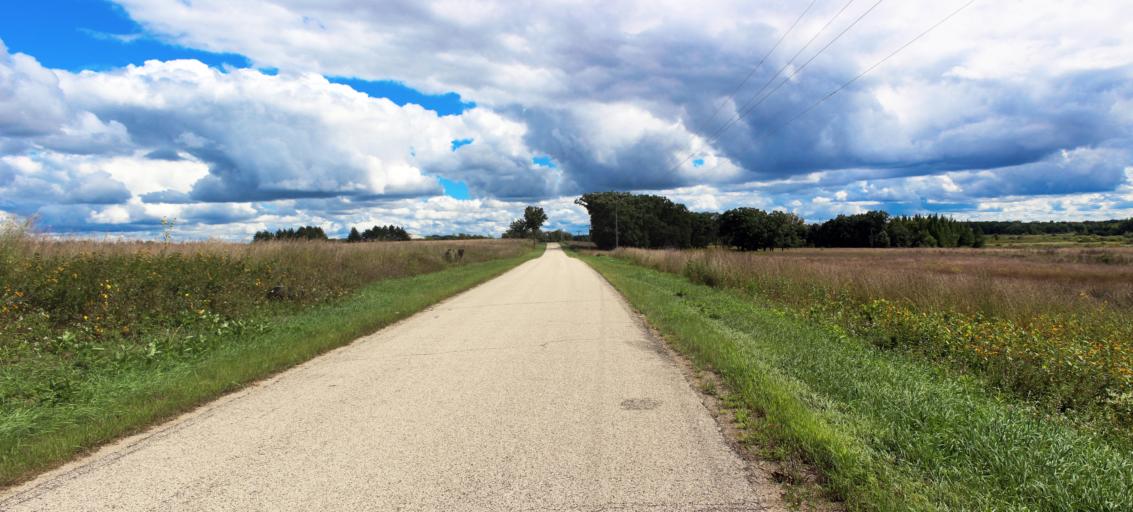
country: US
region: Wisconsin
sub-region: Waushara County
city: Redgranite
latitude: 43.9565
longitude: -89.1278
